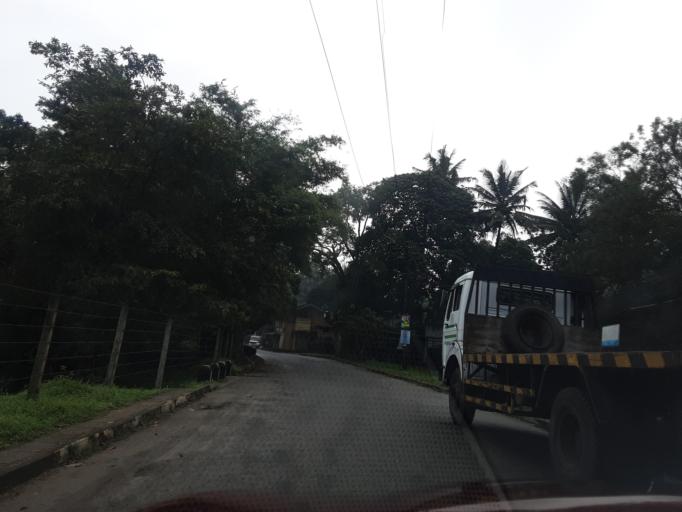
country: LK
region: Central
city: Kandy
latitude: 7.3201
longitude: 80.6235
